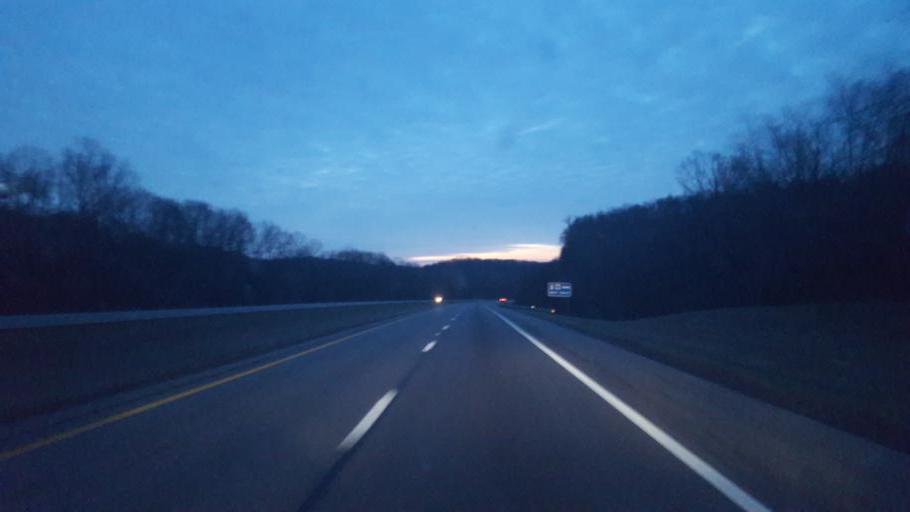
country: US
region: Ohio
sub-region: Jackson County
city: Jackson
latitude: 39.0795
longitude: -82.6349
